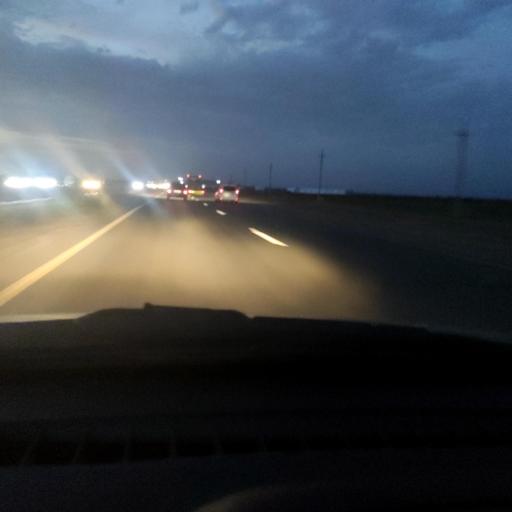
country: RU
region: Samara
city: Zhigulevsk
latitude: 53.5500
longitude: 49.5078
